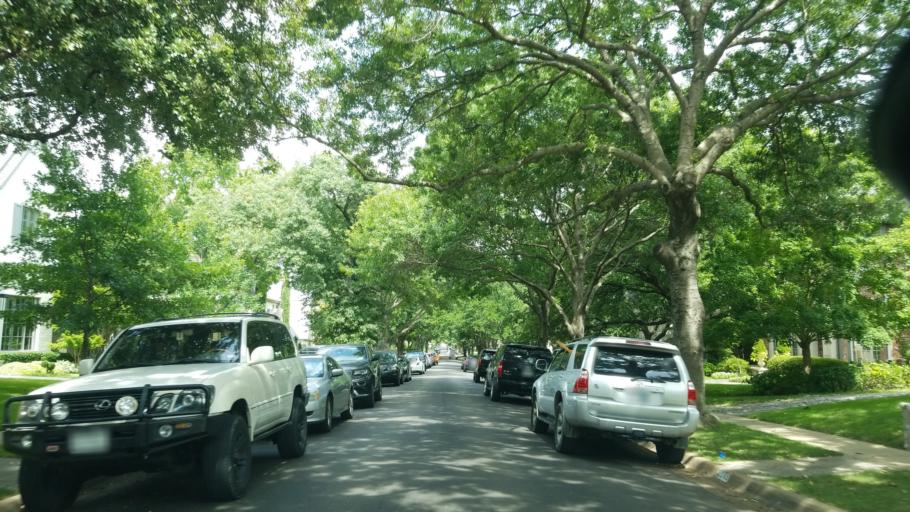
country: US
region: Texas
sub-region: Dallas County
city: University Park
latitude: 32.8539
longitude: -96.8027
